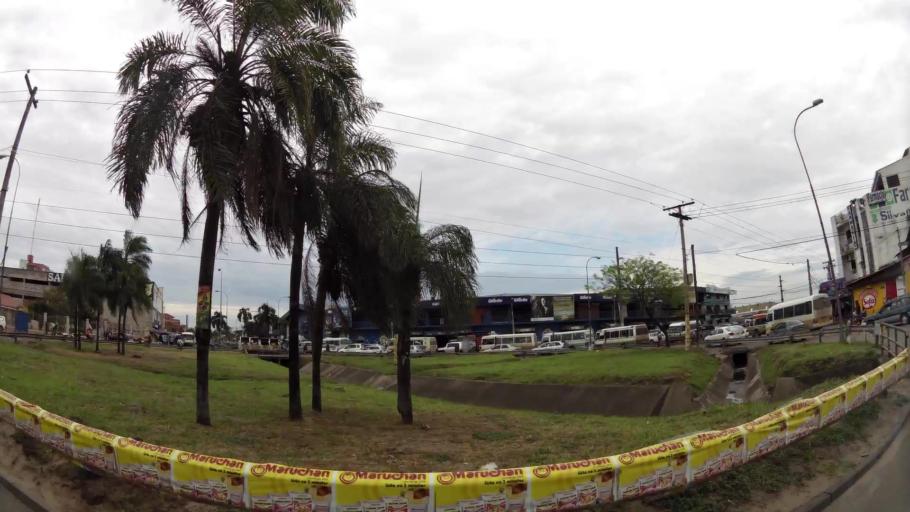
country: BO
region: Santa Cruz
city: Santa Cruz de la Sierra
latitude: -17.7634
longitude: -63.1596
